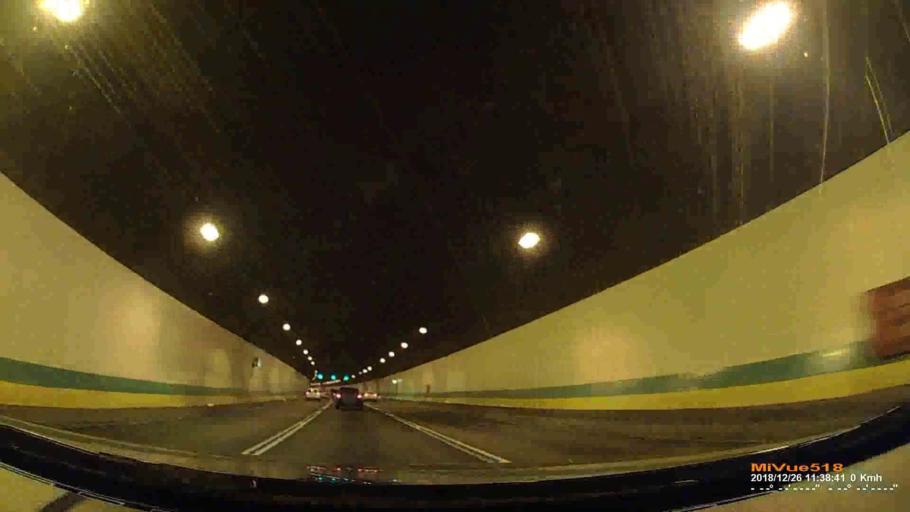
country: TW
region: Taipei
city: Taipei
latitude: 24.9832
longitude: 121.5866
